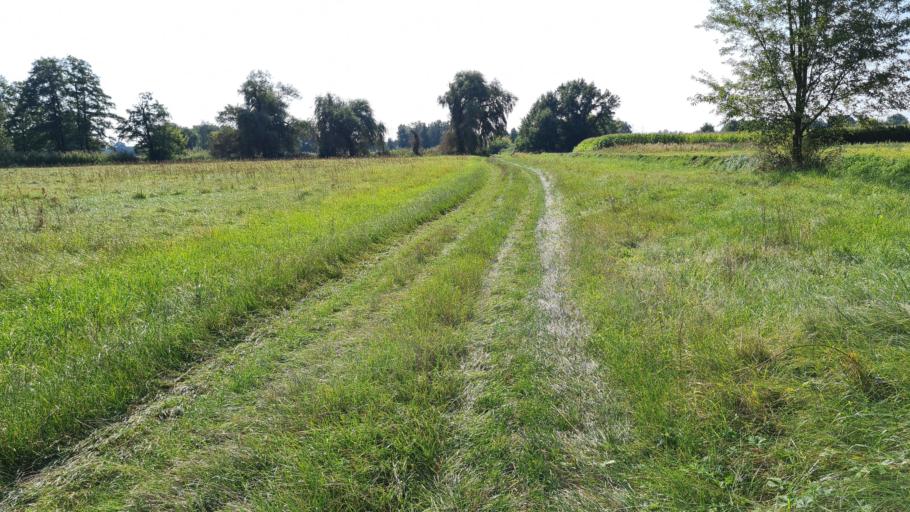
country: DE
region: Brandenburg
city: Bad Liebenwerda
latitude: 51.5035
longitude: 13.4105
